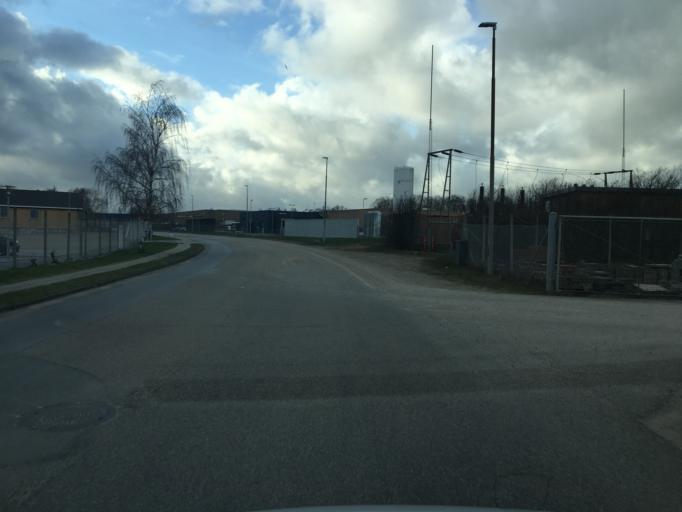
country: DK
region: South Denmark
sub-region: Sonderborg Kommune
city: Grasten
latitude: 54.9121
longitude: 9.5980
